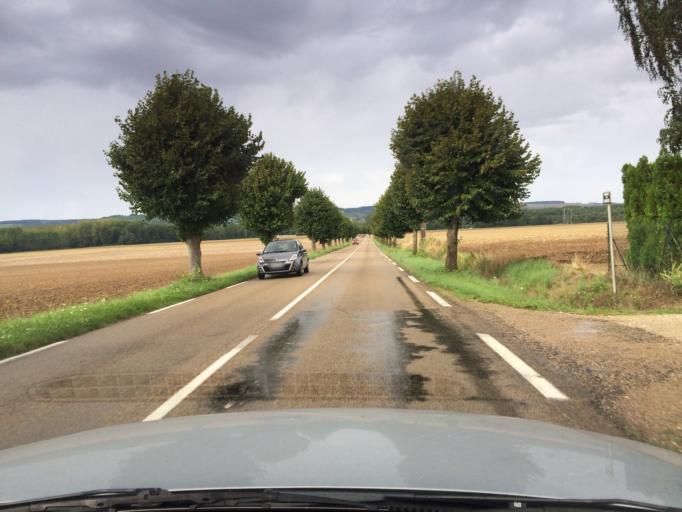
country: FR
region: Bourgogne
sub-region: Departement de l'Yonne
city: Joigny
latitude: 47.9575
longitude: 3.3780
